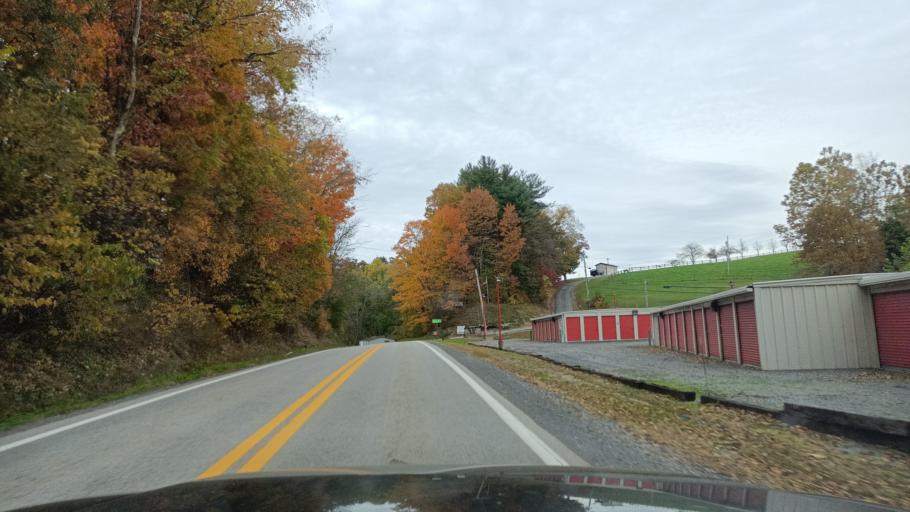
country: US
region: West Virginia
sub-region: Taylor County
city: Grafton
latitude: 39.3726
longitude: -79.9713
